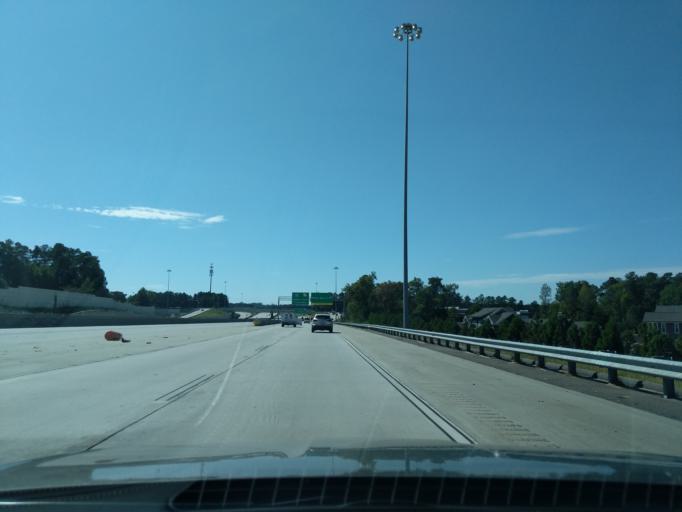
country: US
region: Georgia
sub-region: Columbia County
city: Martinez
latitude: 33.4974
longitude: -82.0745
